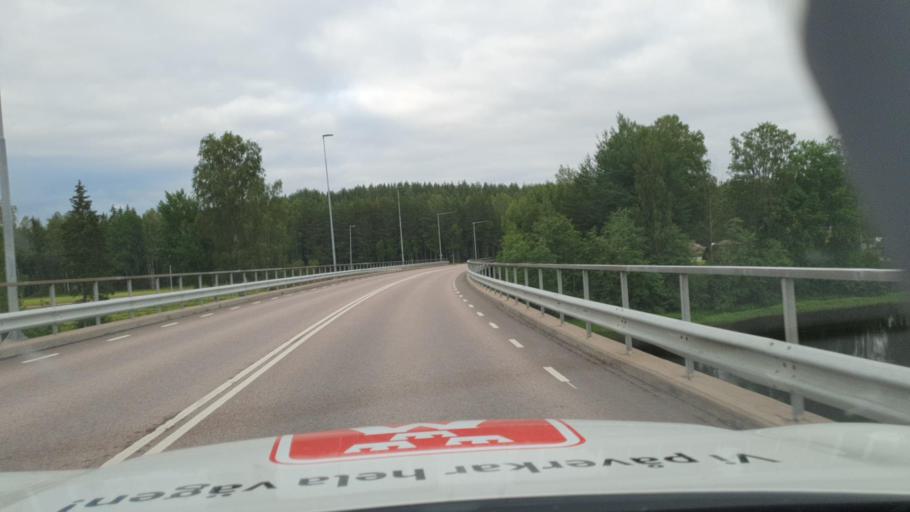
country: SE
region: Vaermland
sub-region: Karlstads Kommun
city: Karlstad
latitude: 59.4283
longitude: 13.4550
